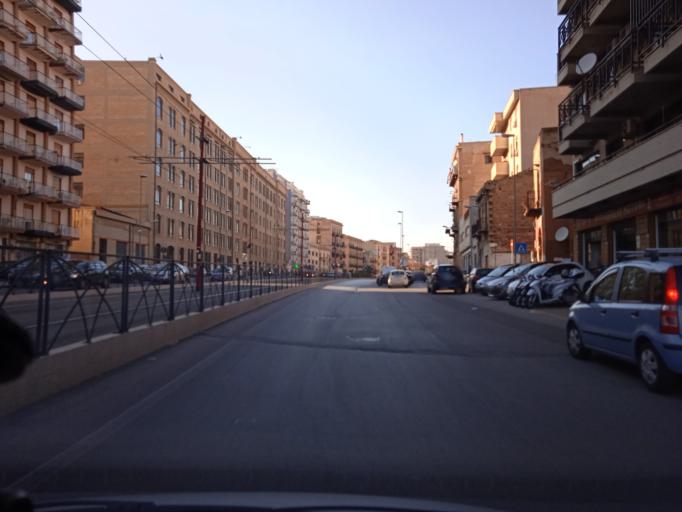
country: IT
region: Sicily
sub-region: Palermo
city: Palermo
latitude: 38.1072
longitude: 13.3727
